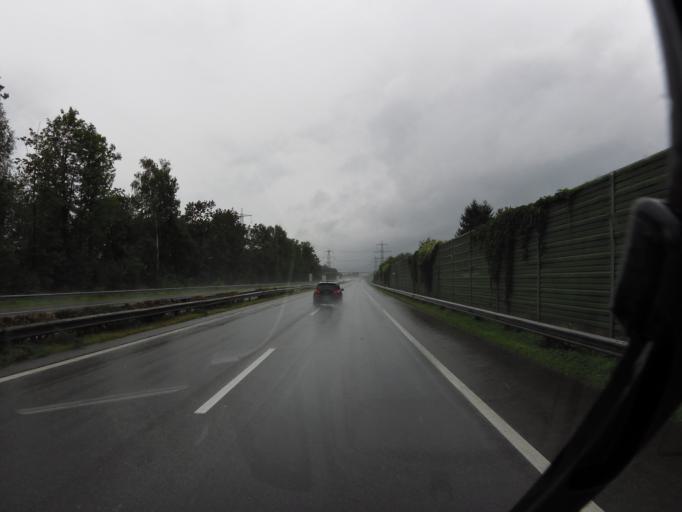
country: AT
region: Vorarlberg
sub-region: Politischer Bezirk Feldkirch
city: Altach
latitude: 47.3616
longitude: 9.6491
